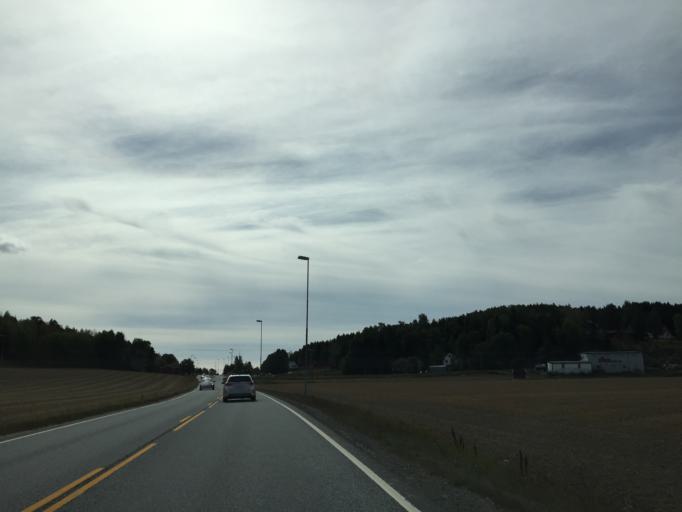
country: NO
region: Ostfold
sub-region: Fredrikstad
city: Fredrikstad
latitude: 59.2501
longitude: 10.8957
